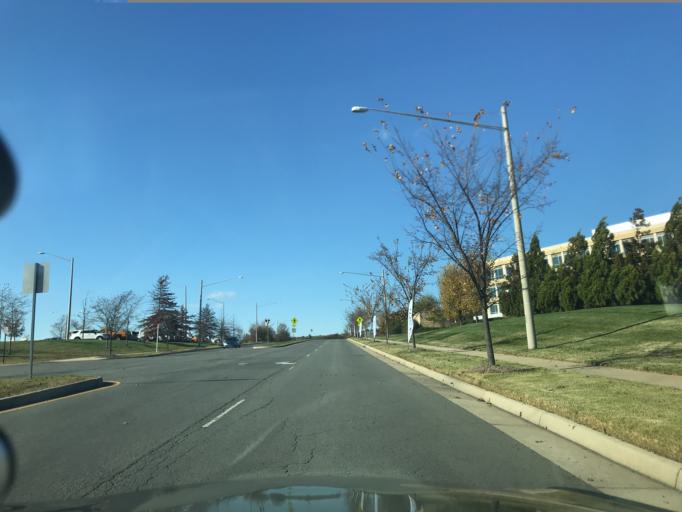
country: US
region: Virginia
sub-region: Fairfax County
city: Greenbriar
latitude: 38.8481
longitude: -77.3742
